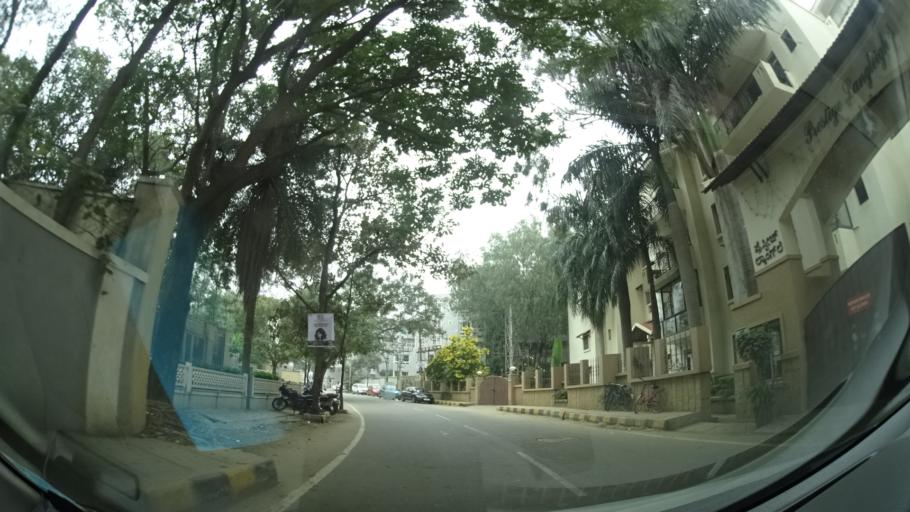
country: IN
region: Karnataka
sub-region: Bangalore Rural
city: Hoskote
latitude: 12.9824
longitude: 77.7439
